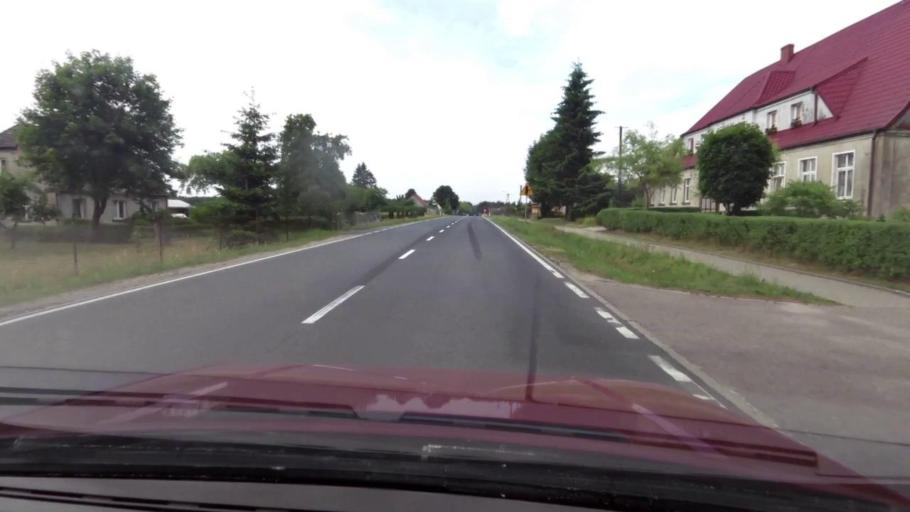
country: PL
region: Pomeranian Voivodeship
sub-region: Powiat bytowski
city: Trzebielino
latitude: 54.2448
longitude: 17.0976
